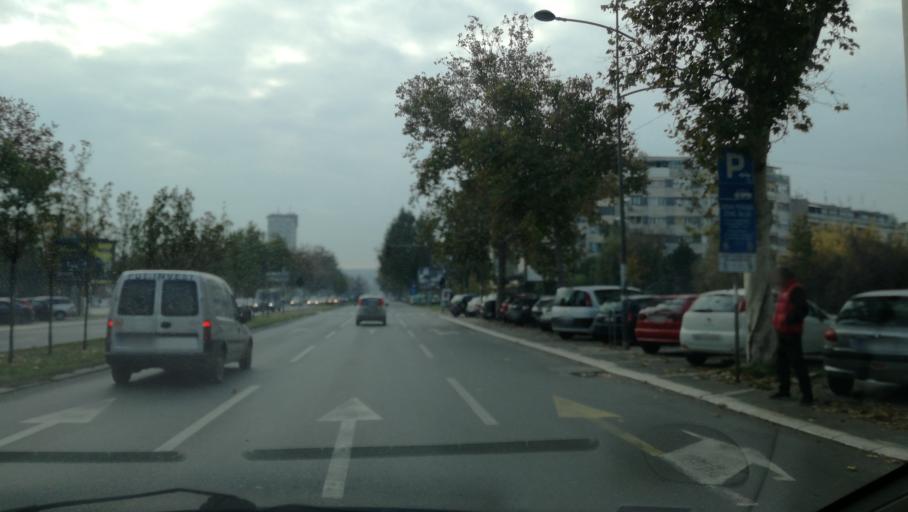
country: RS
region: Autonomna Pokrajina Vojvodina
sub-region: Juznobacki Okrug
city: Novi Sad
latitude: 45.2473
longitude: 19.8395
